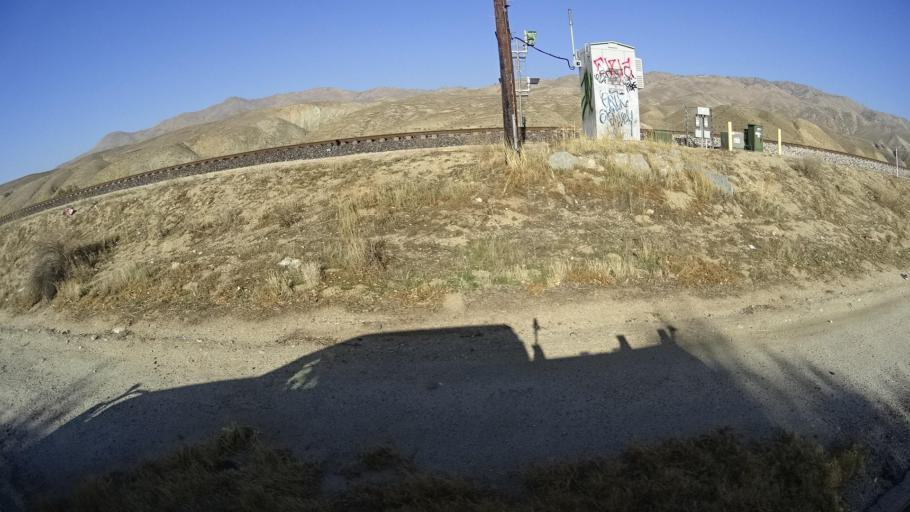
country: US
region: California
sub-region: Kern County
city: Arvin
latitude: 35.3217
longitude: -118.7124
